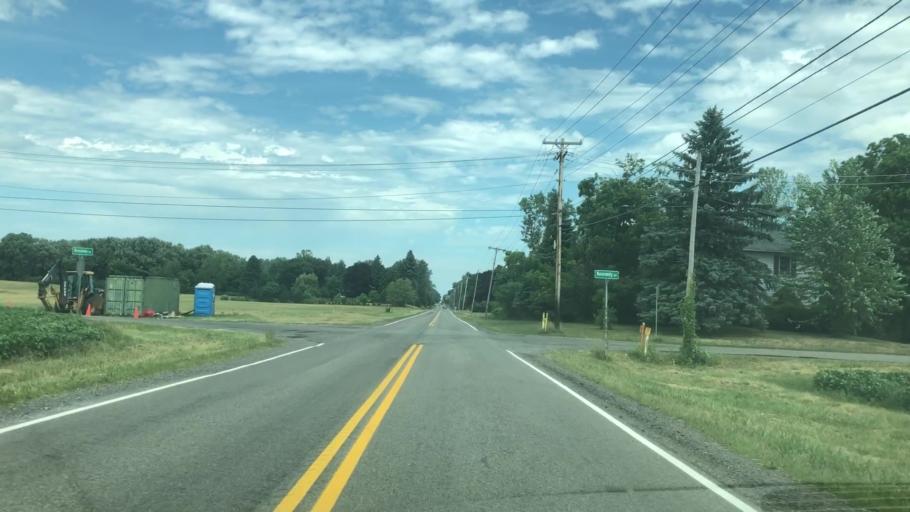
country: US
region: New York
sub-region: Monroe County
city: Webster
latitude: 43.1738
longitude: -77.4005
